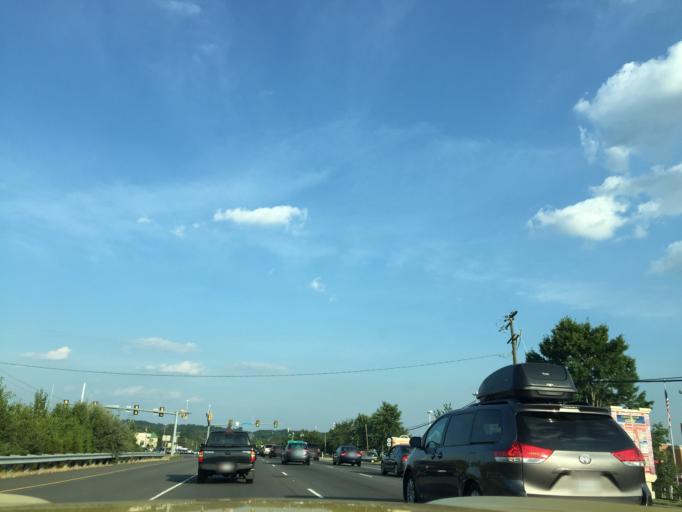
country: US
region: Virginia
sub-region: Loudoun County
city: Sugarland Run
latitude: 39.0170
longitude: -77.3765
